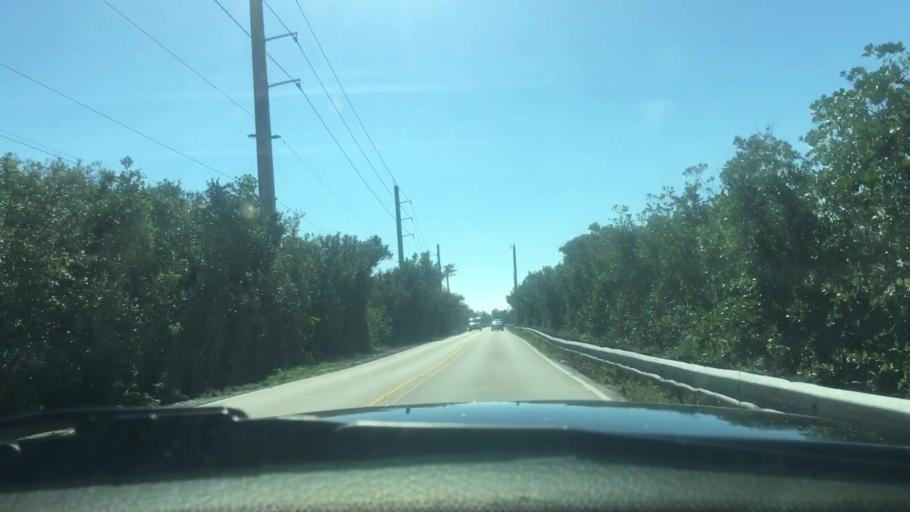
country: US
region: Florida
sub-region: Monroe County
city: North Key Largo
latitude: 25.2992
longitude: -80.3863
